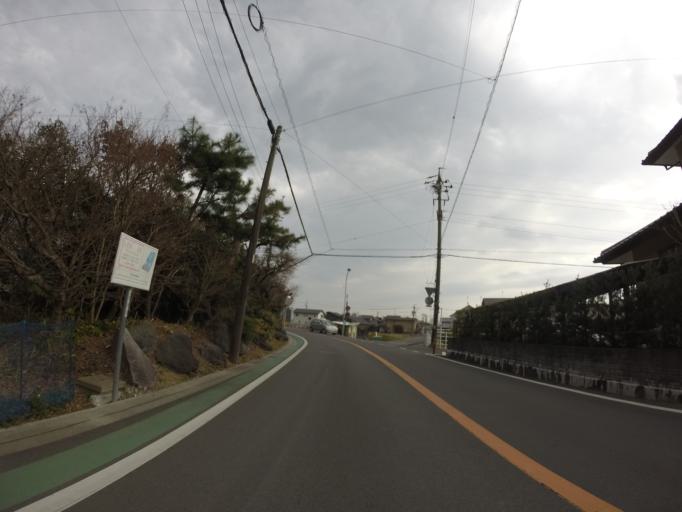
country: JP
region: Shizuoka
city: Shizuoka-shi
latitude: 35.0419
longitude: 138.4574
